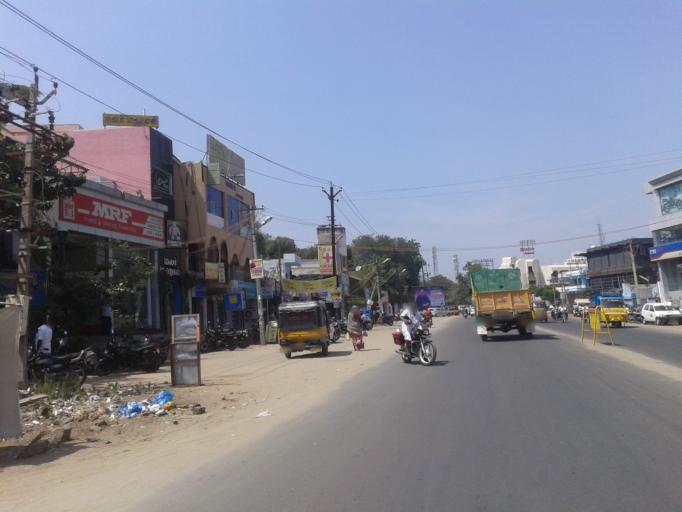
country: IN
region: Tamil Nadu
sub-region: Madurai
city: Madurai
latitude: 9.9329
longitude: 78.0925
